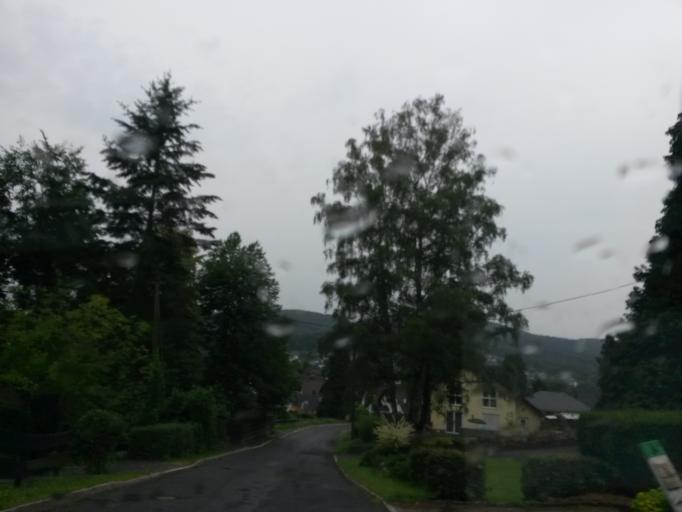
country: DE
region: North Rhine-Westphalia
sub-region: Regierungsbezirk Koln
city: Engelskirchen
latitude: 50.9688
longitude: 7.3638
